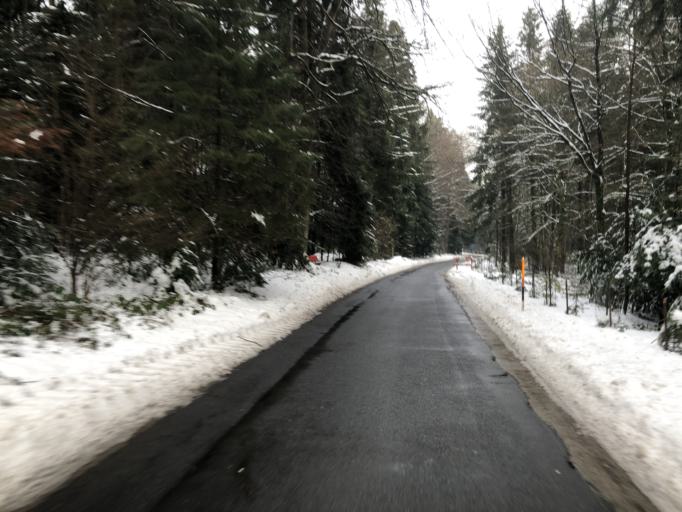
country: CH
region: Bern
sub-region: Oberaargau
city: Lotzwil
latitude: 47.2035
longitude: 7.7691
